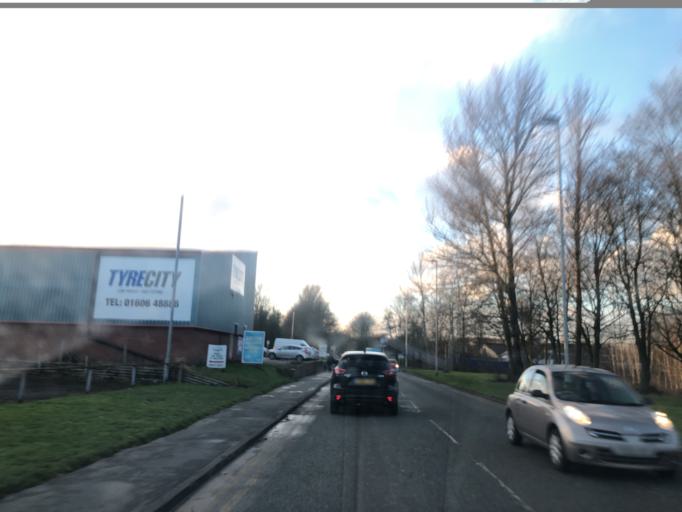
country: GB
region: England
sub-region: Cheshire West and Chester
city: Marston
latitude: 53.2640
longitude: -2.5033
